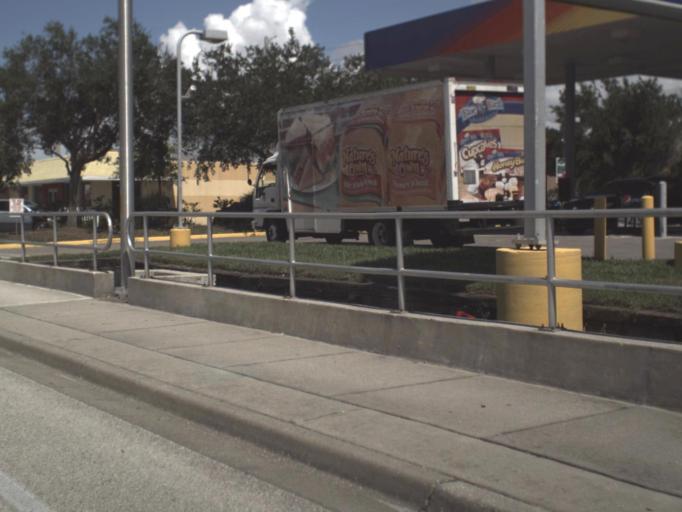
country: US
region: Florida
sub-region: Sarasota County
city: Venice Gardens
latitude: 27.0666
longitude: -82.4195
